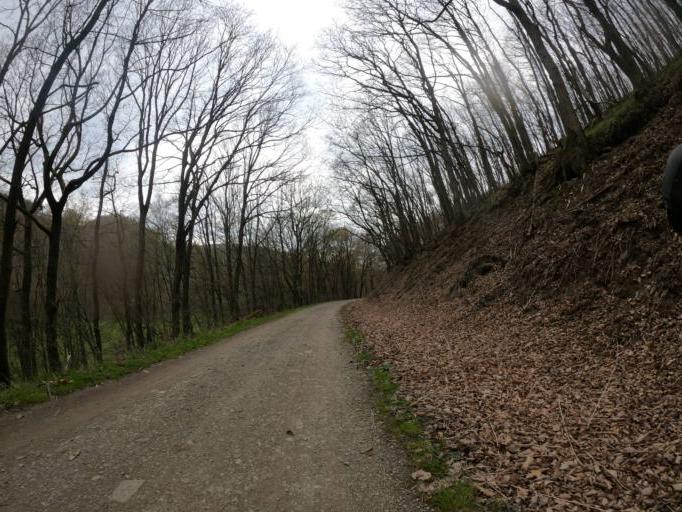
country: DE
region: North Rhine-Westphalia
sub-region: Regierungsbezirk Koln
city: Nideggen
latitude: 50.6816
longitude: 6.4215
